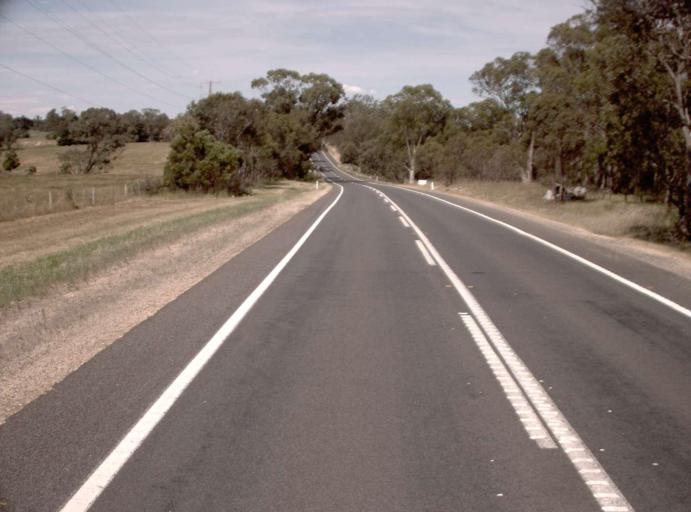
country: AU
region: Victoria
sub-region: East Gippsland
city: Bairnsdale
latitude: -37.9010
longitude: 147.3538
